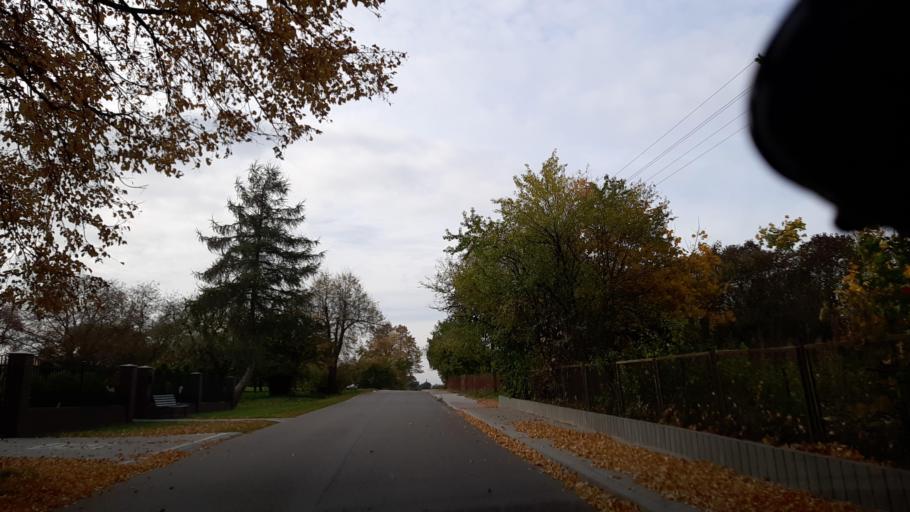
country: PL
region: Lublin Voivodeship
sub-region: Powiat lubelski
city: Garbow
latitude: 51.3836
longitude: 22.3784
